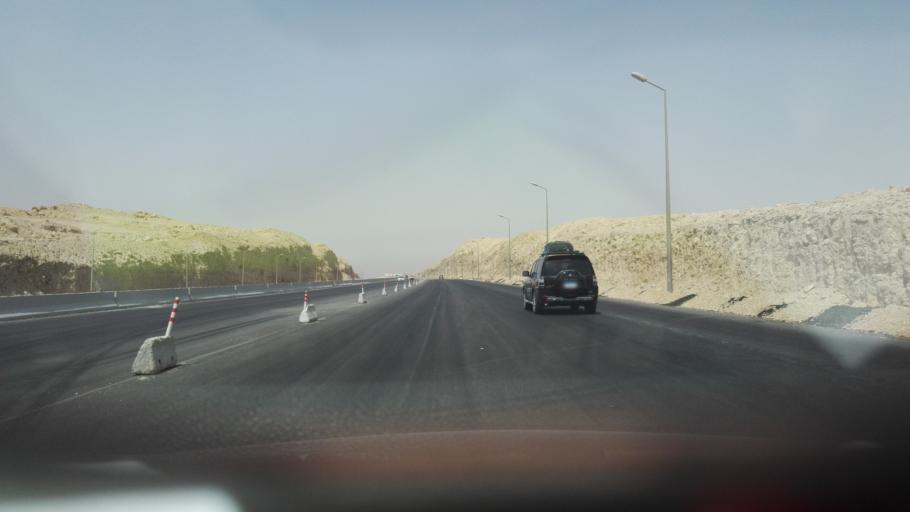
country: EG
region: As Suways
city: Ain Sukhna
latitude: 29.6814
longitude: 32.2166
